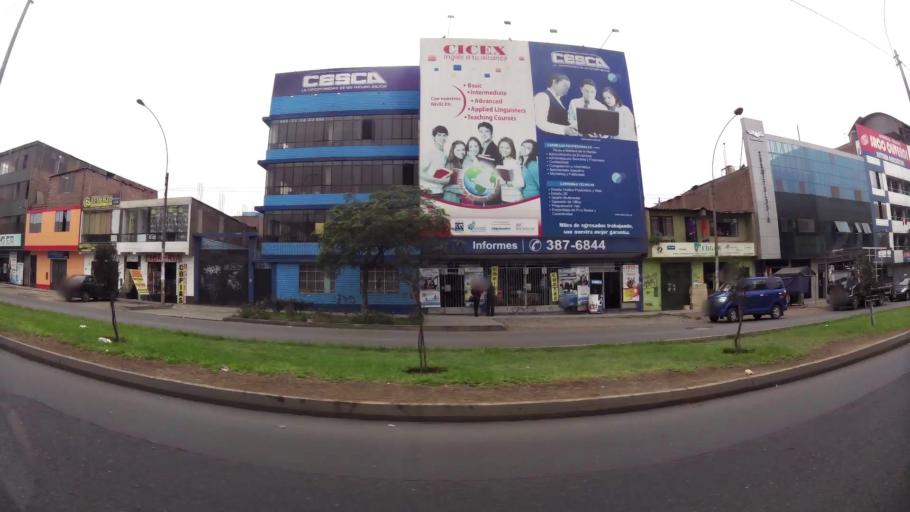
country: PE
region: Lima
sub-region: Lima
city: Independencia
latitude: -11.9740
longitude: -76.9993
